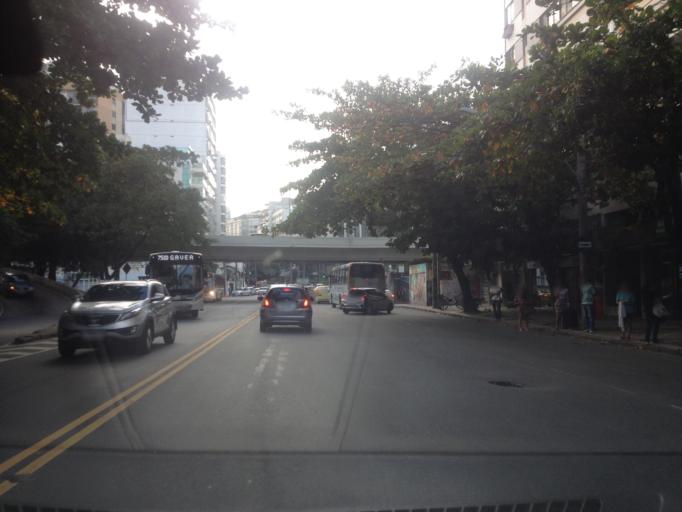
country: BR
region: Rio de Janeiro
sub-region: Rio De Janeiro
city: Rio de Janeiro
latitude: -22.9604
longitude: -43.2050
